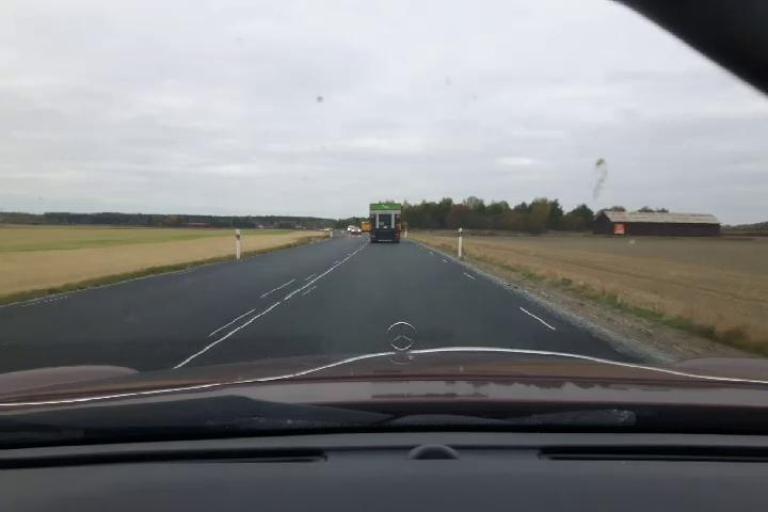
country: SE
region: Uppsala
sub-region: Enkopings Kommun
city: Enkoping
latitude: 59.6270
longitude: 17.0470
